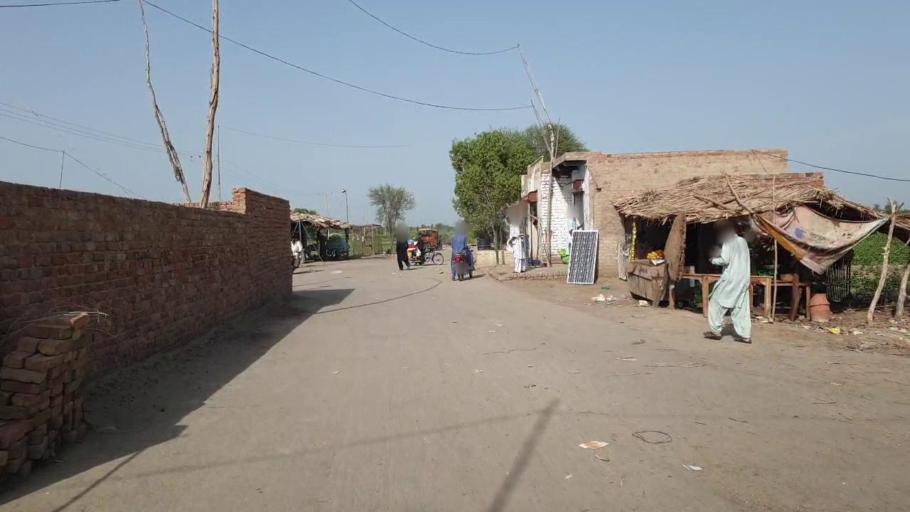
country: PK
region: Sindh
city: Sakrand
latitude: 26.2846
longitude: 68.2262
